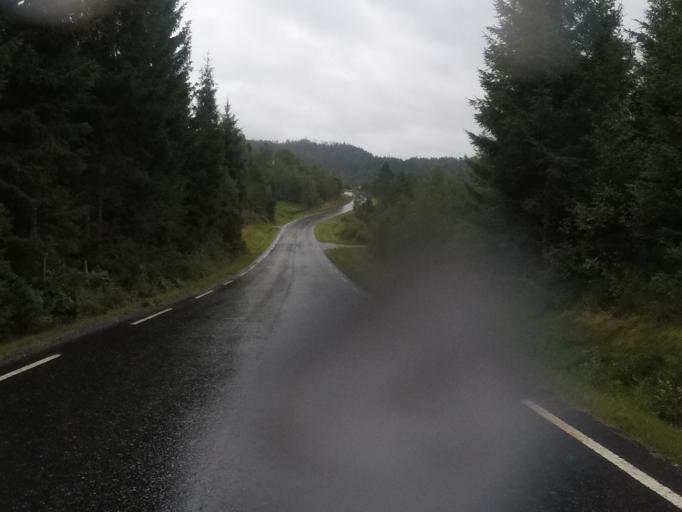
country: NO
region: Vest-Agder
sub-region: Audnedal
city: Konsmo
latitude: 58.2775
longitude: 7.2819
